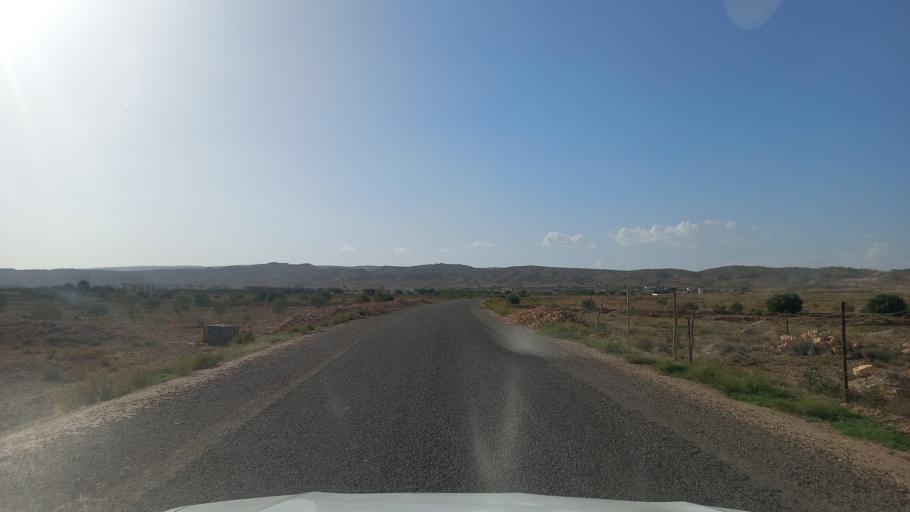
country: TN
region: Al Qasrayn
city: Sbiba
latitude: 35.3391
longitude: 8.9973
